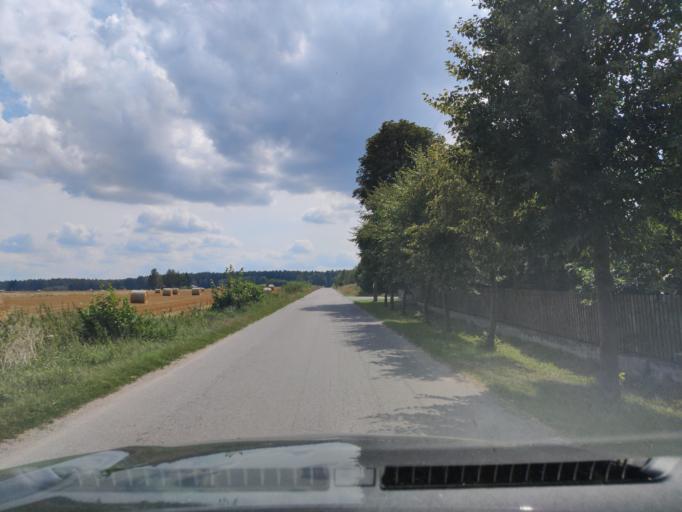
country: PL
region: Masovian Voivodeship
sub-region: Powiat pultuski
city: Obryte
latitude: 52.7124
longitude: 21.2421
